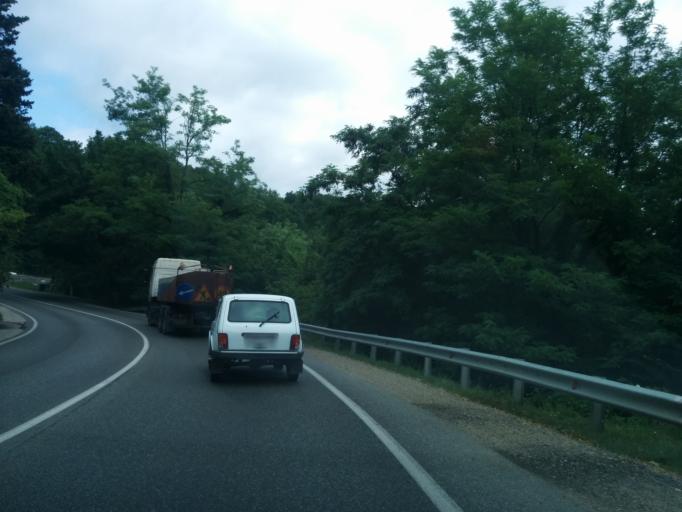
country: RU
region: Krasnodarskiy
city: Agoy
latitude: 44.1196
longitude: 39.0496
